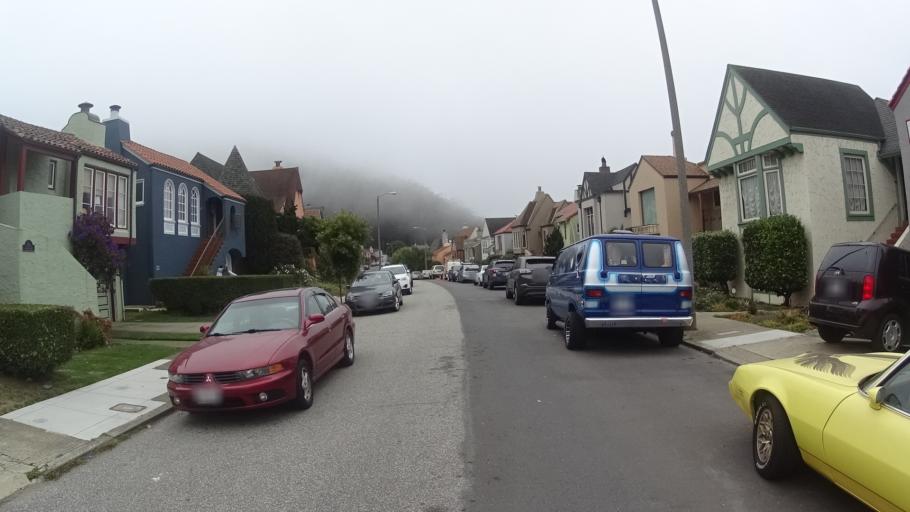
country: US
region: California
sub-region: San Mateo County
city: Daly City
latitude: 37.7429
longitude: -122.4542
